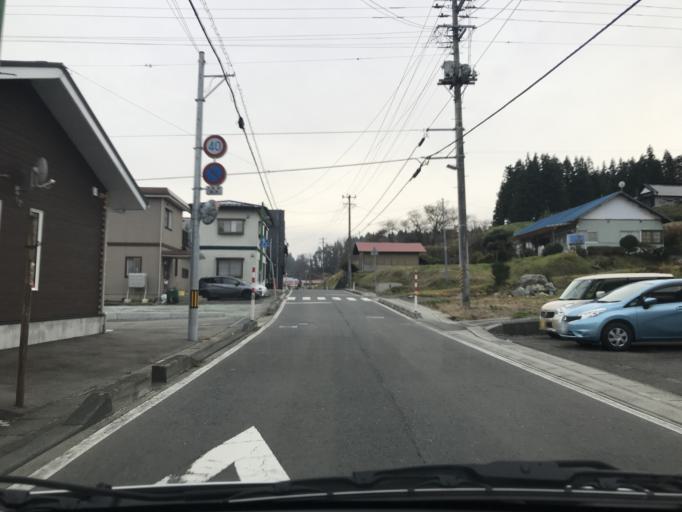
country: JP
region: Iwate
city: Kitakami
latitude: 39.2871
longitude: 141.2621
